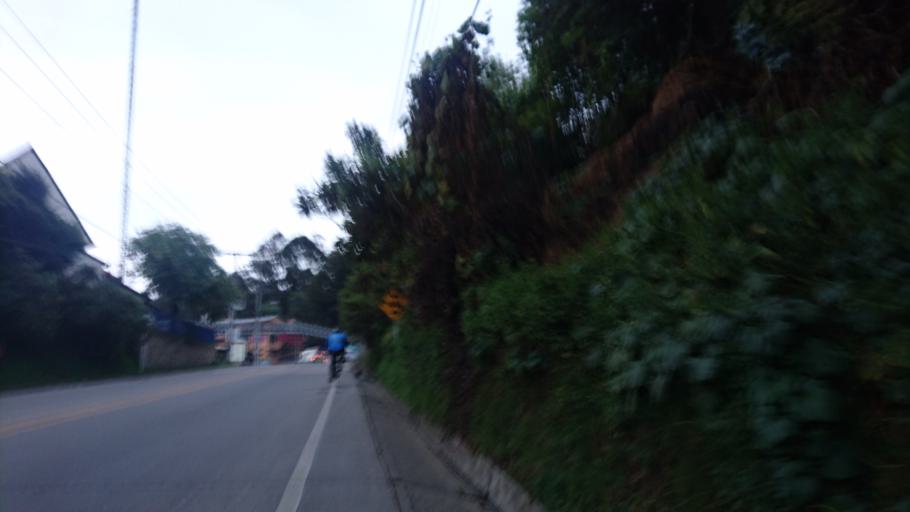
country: CO
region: Bogota D.C.
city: Barrio San Luis
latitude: 4.6713
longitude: -74.0166
